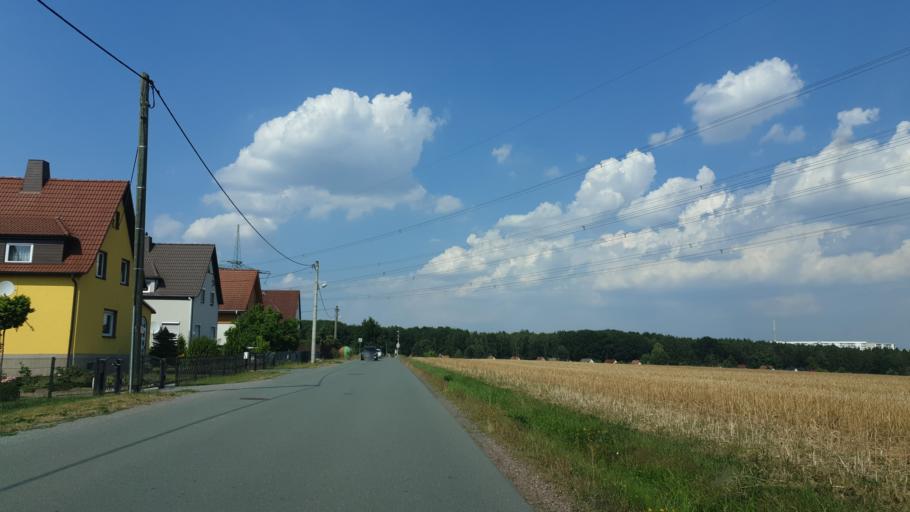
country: DE
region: Saxony
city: Neukirchen
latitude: 50.7774
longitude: 12.8865
